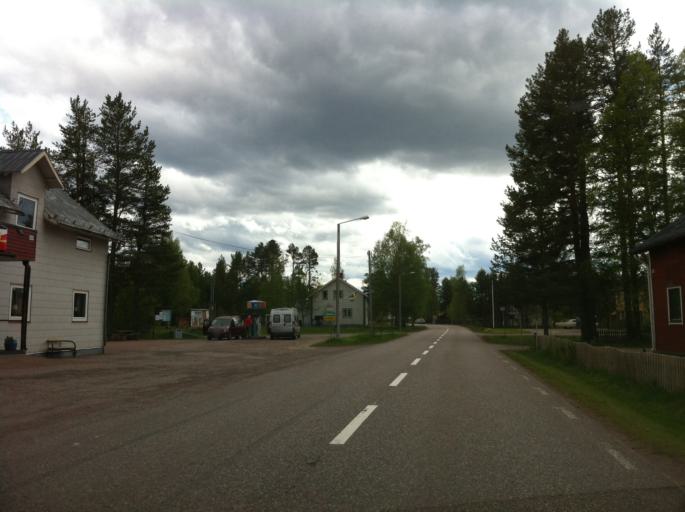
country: NO
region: Hedmark
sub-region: Trysil
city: Innbygda
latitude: 61.4109
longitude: 13.0836
